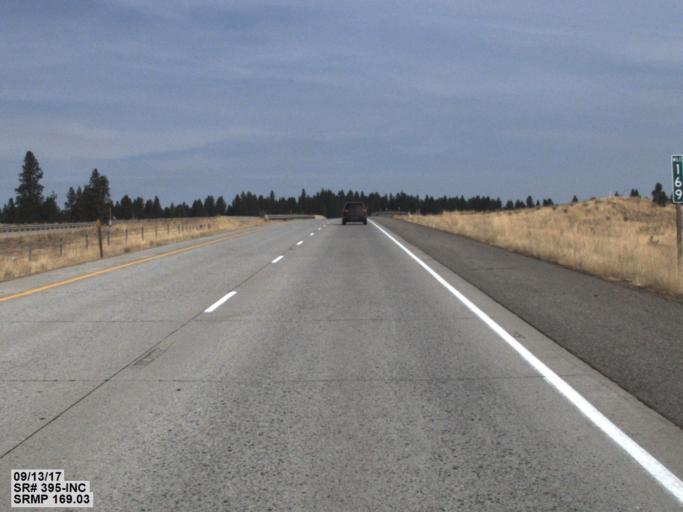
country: US
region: Washington
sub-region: Spokane County
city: Fairwood
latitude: 47.8031
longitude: -117.4057
